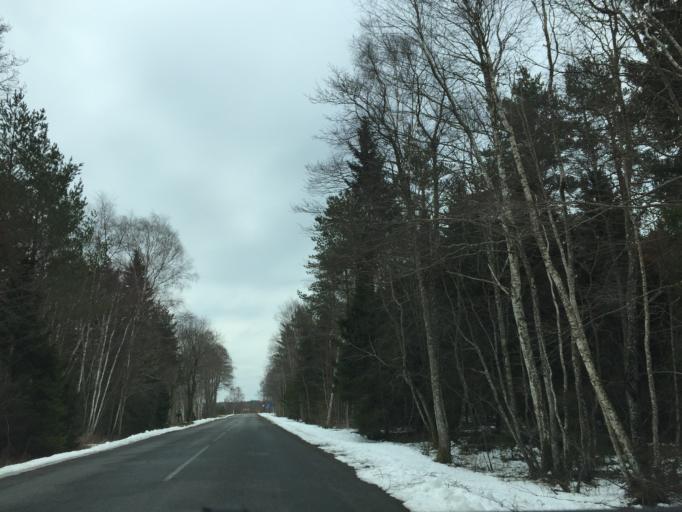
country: EE
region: Saare
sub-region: Kuressaare linn
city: Kuressaare
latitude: 58.4183
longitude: 22.1275
